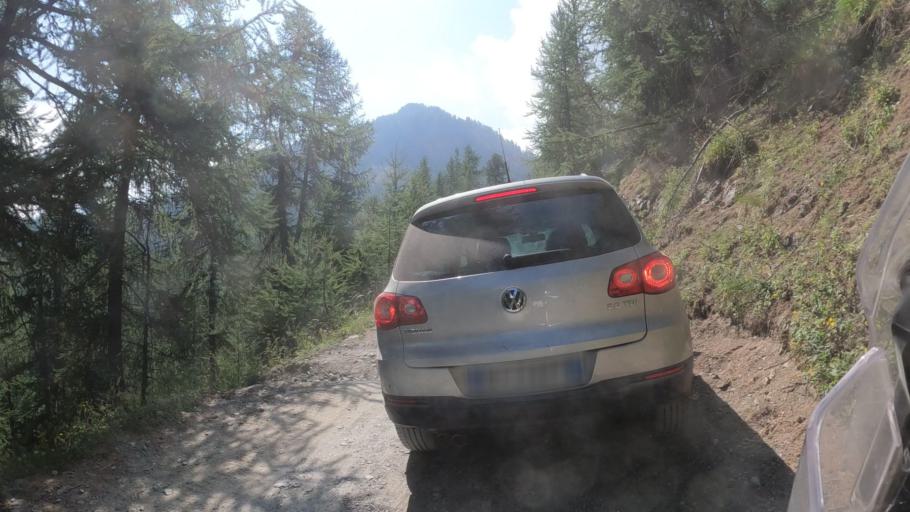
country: IT
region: Piedmont
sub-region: Provincia di Torino
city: Cesana Torinese
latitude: 44.9119
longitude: 6.7996
